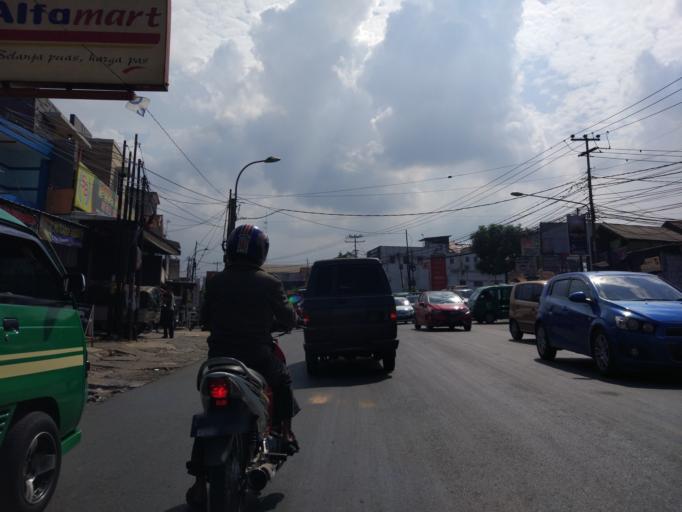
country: ID
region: West Java
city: Cileunyi
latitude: -6.9332
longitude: 107.7266
